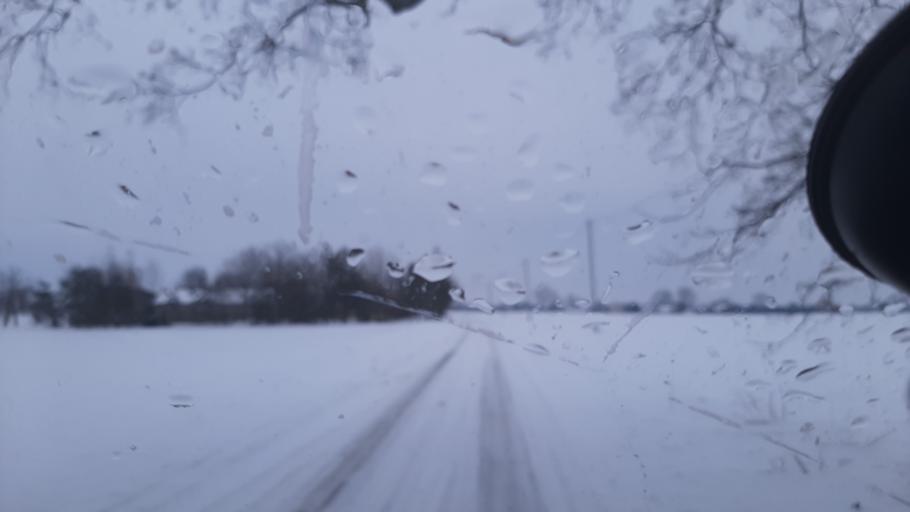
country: PL
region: Lublin Voivodeship
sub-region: Powiat lubelski
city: Garbow
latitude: 51.3560
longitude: 22.3866
